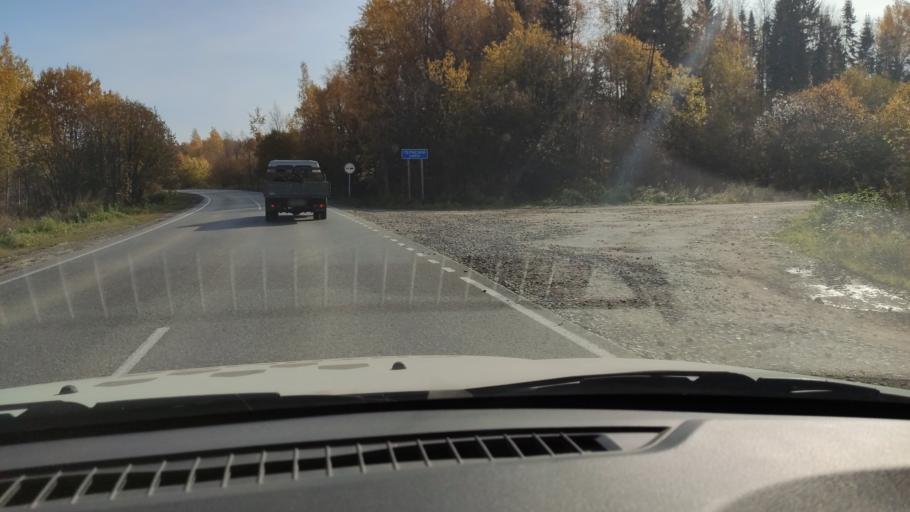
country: RU
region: Perm
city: Novyye Lyady
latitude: 58.0213
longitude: 56.6464
